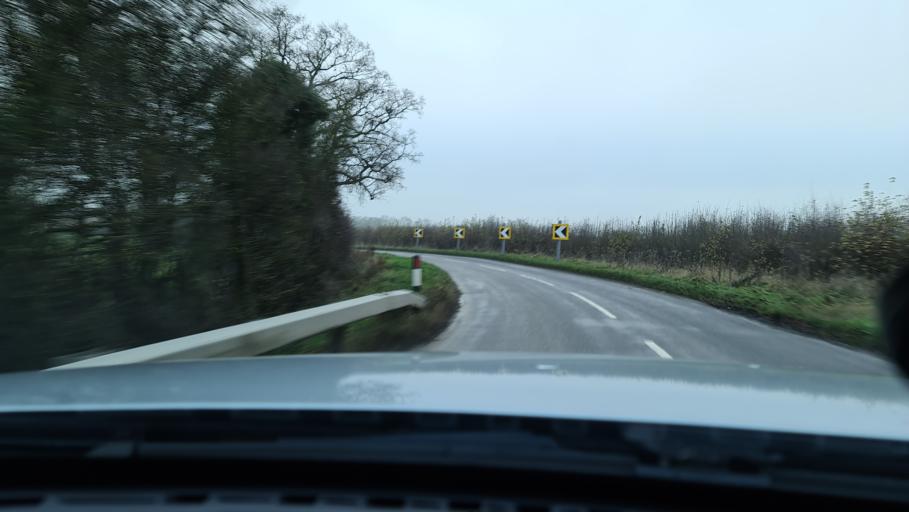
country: GB
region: England
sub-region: Oxfordshire
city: Bicester
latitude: 51.8907
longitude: -1.1088
